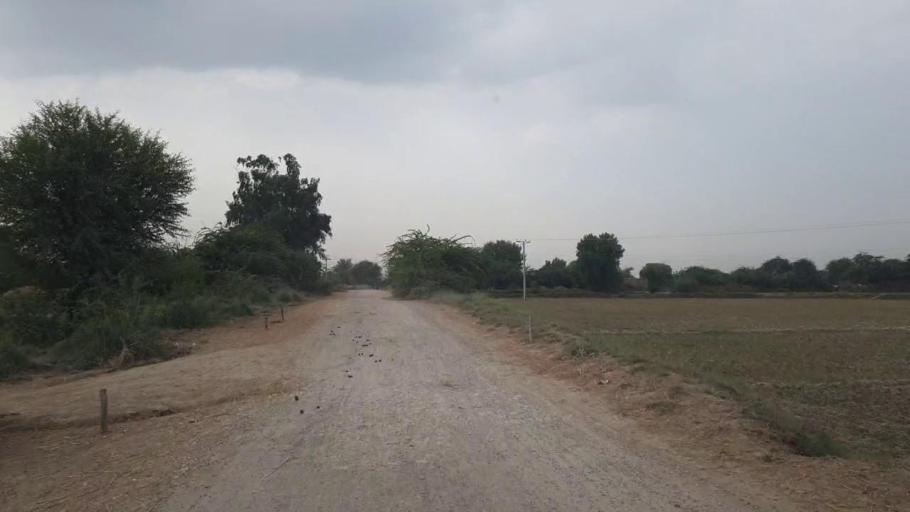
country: PK
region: Sindh
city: Talhar
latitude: 24.9100
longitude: 68.7721
